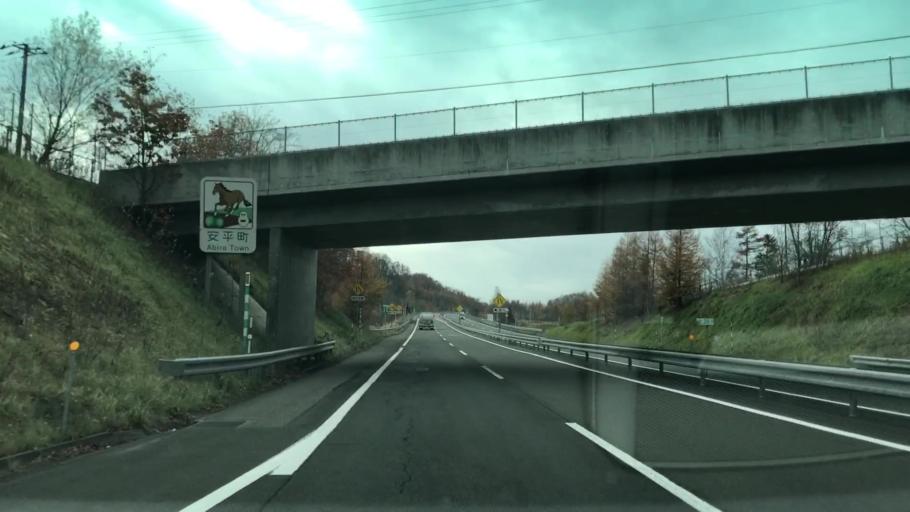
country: JP
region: Hokkaido
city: Chitose
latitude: 42.9051
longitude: 141.8968
